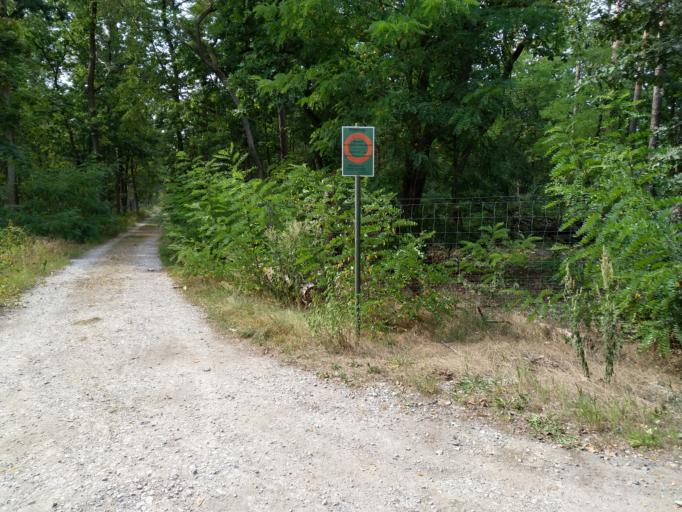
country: DE
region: Berlin
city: Friedrichshagen
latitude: 52.4683
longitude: 13.6209
